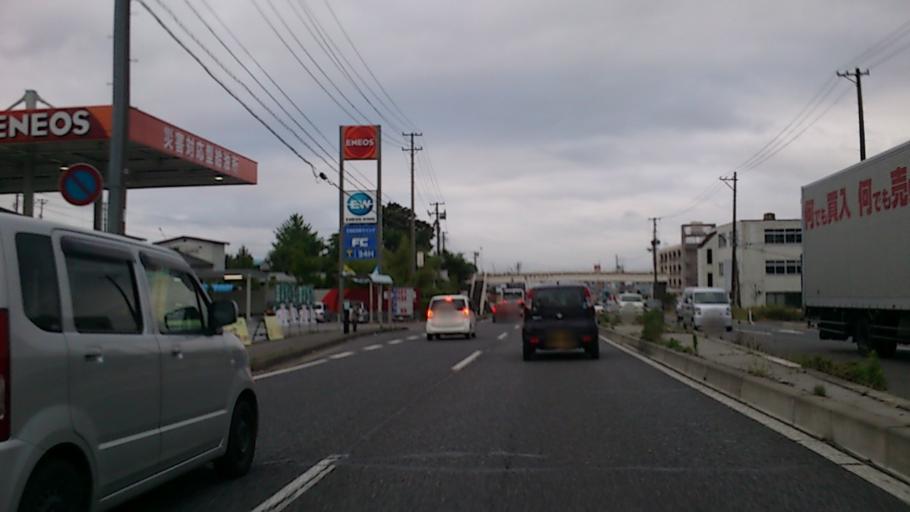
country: JP
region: Fukushima
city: Sukagawa
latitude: 37.3076
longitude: 140.3666
